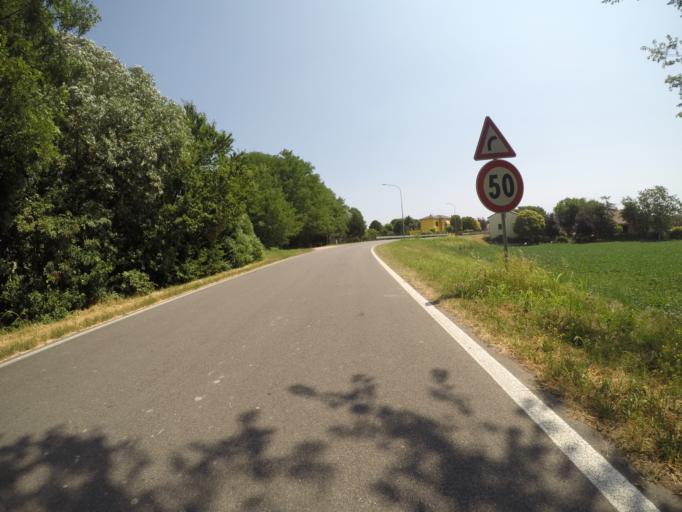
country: IT
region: Veneto
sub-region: Provincia di Rovigo
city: Villamarzana
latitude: 45.0079
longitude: 11.6702
